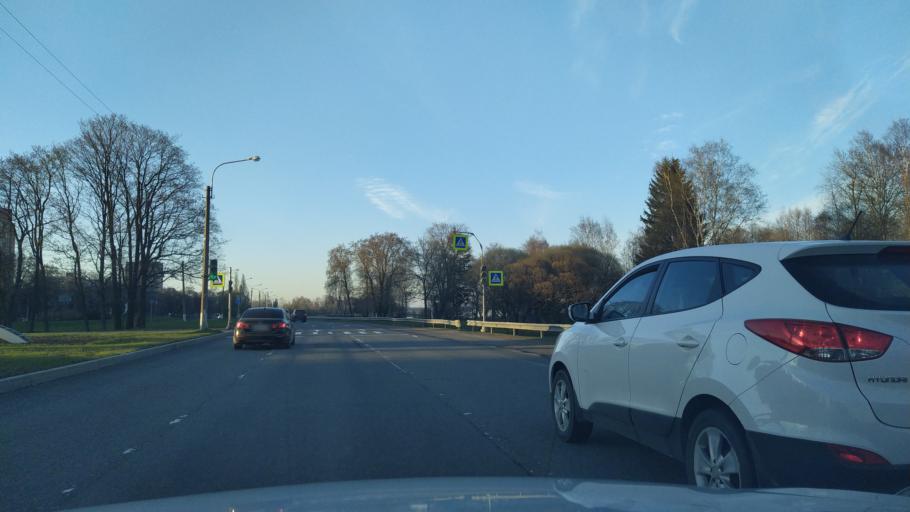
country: RU
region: St.-Petersburg
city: Sestroretsk
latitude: 60.0929
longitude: 29.9764
